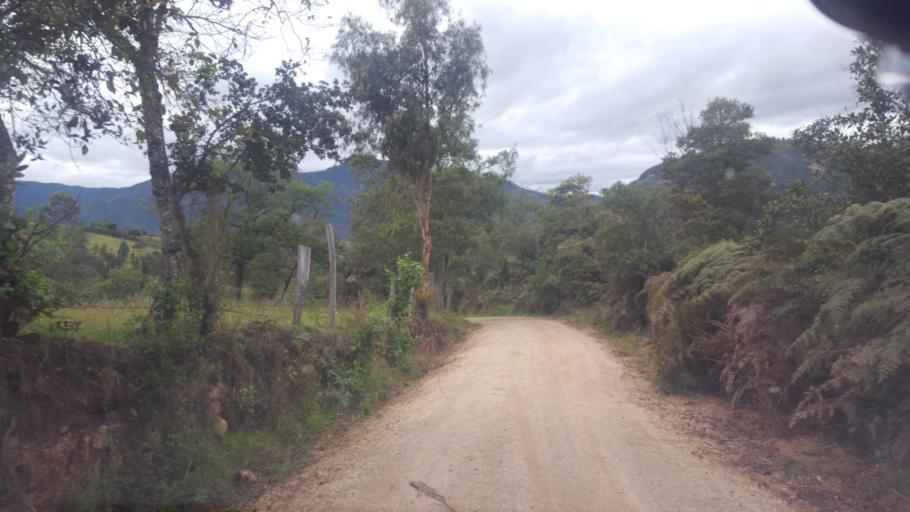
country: CO
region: Boyaca
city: Cerinza
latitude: 5.9912
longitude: -72.9501
